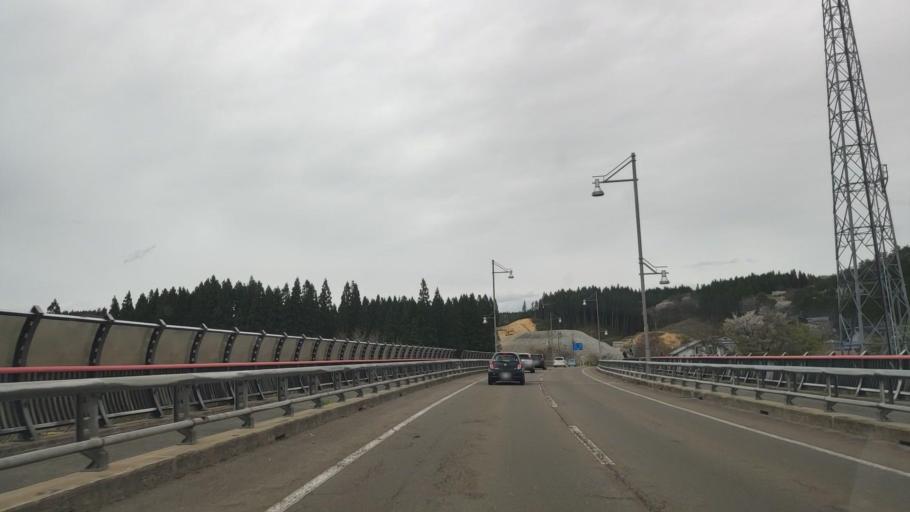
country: JP
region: Akita
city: Takanosu
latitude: 40.2106
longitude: 140.3018
